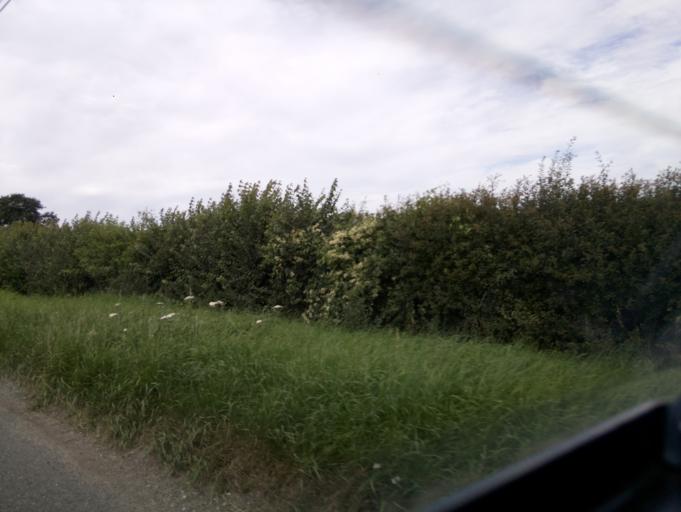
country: GB
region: England
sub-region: Somerset
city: Ilchester
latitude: 51.0681
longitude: -2.6826
